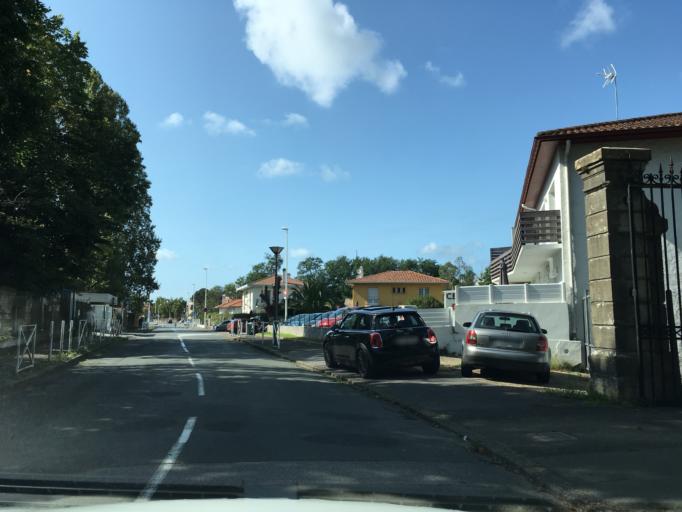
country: FR
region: Aquitaine
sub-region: Departement des Pyrenees-Atlantiques
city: Bayonne
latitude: 43.4801
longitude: -1.4784
